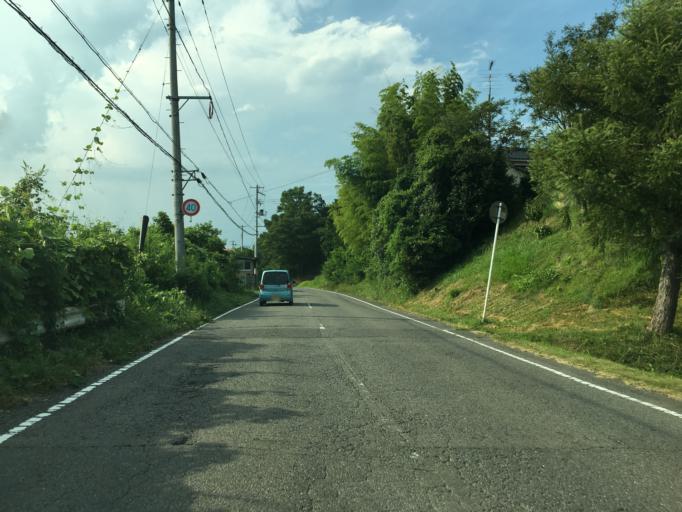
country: JP
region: Fukushima
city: Miharu
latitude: 37.4558
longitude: 140.4263
